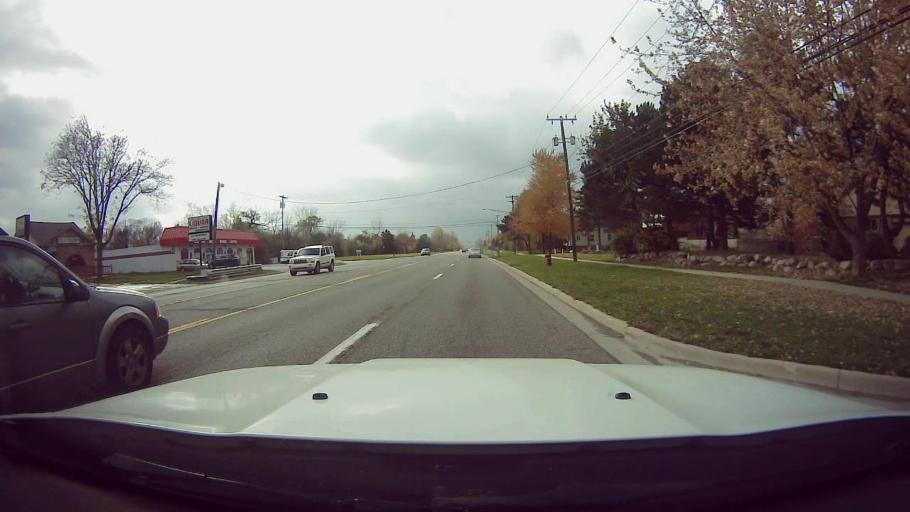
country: US
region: Michigan
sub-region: Oakland County
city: Clawson
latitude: 42.5493
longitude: -83.0975
